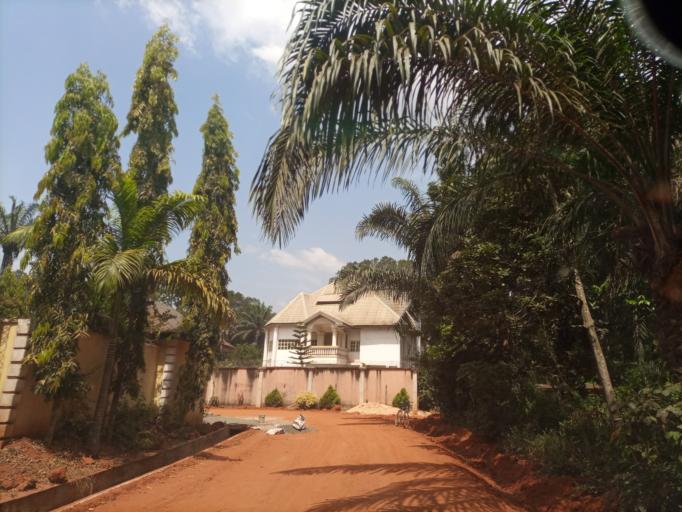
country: NG
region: Enugu
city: Obollo-Afor
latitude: 6.8665
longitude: 7.4733
